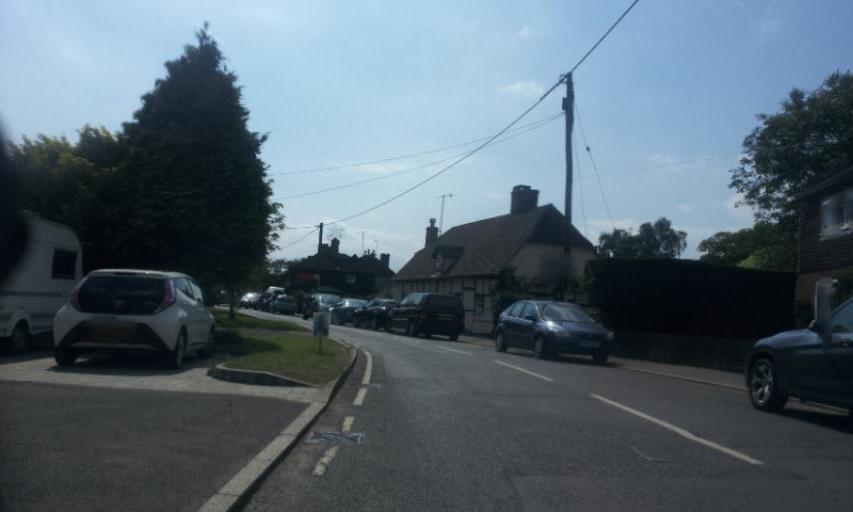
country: GB
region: England
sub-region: Kent
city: Teynham
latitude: 51.2848
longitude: 0.8025
